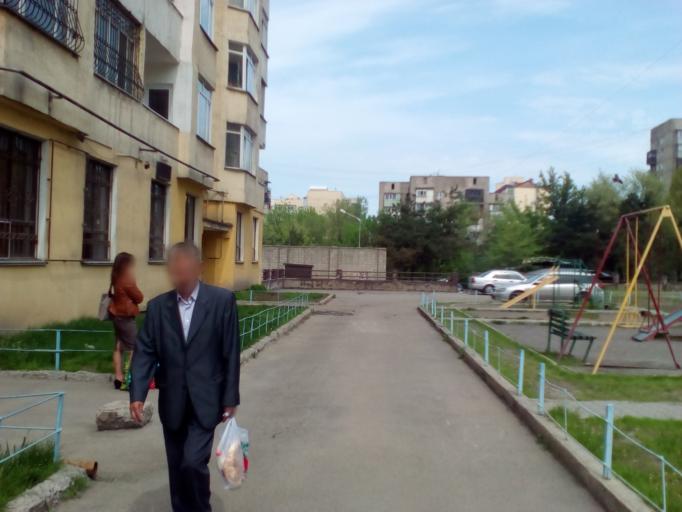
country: KZ
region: Almaty Qalasy
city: Almaty
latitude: 43.2373
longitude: 76.8262
